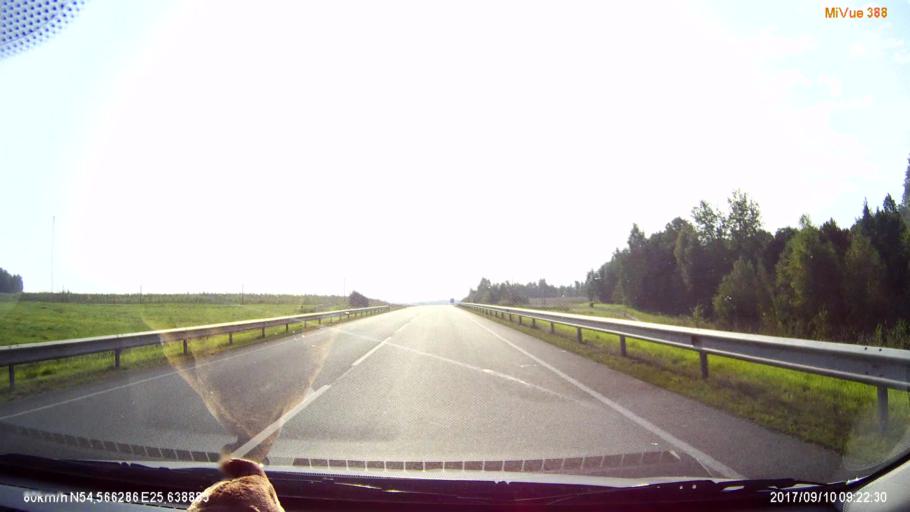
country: LT
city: Skaidiskes
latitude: 54.5661
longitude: 25.6398
